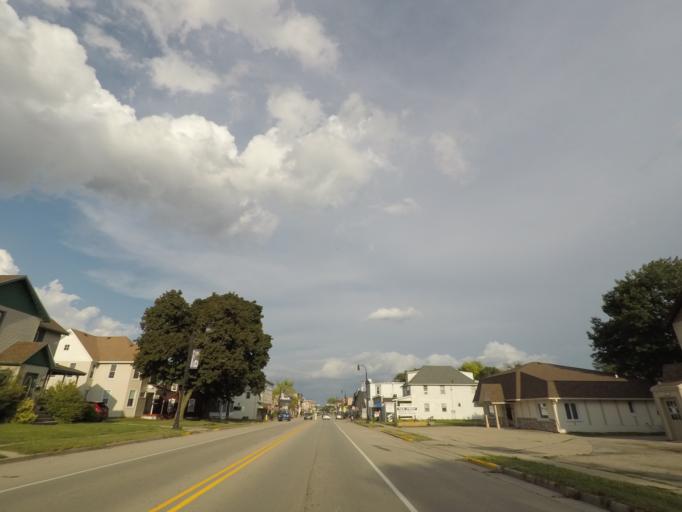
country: US
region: Wisconsin
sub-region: Dane County
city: Waunakee
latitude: 43.1920
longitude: -89.4580
